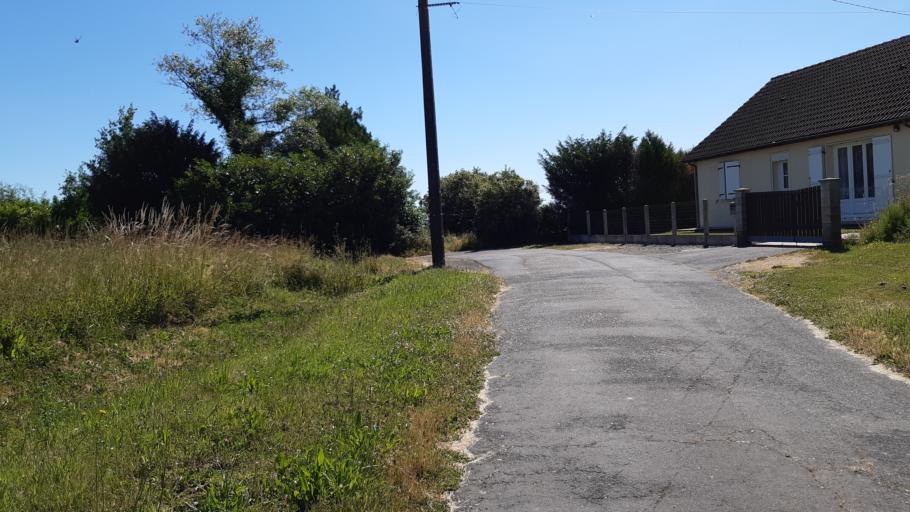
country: FR
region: Centre
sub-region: Departement d'Indre-et-Loire
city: Mettray
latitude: 47.4311
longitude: 0.6567
